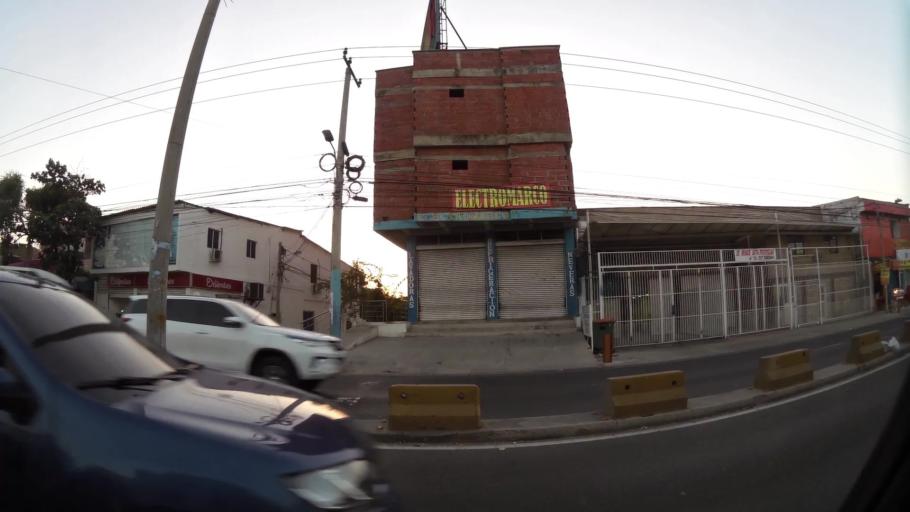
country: CO
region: Bolivar
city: Cartagena
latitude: 10.4030
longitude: -75.5197
